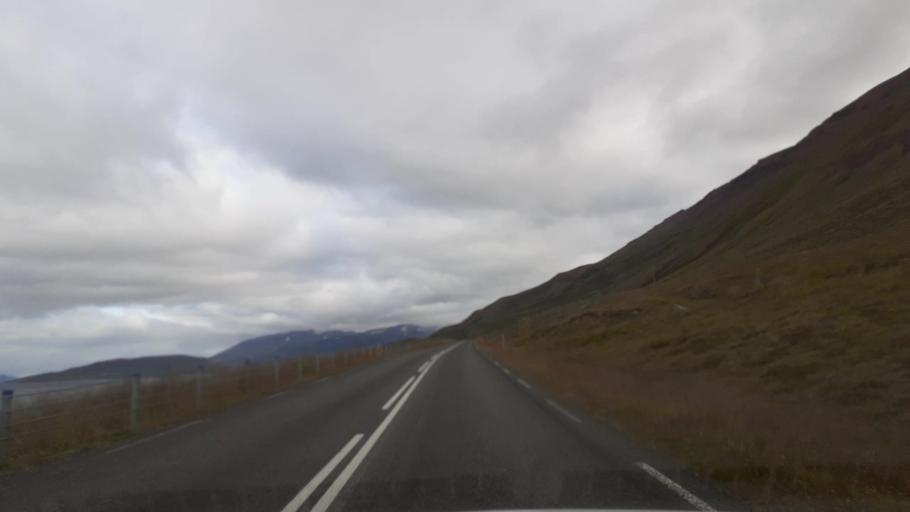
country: IS
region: Northeast
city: Akureyri
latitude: 65.8490
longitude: -18.0597
